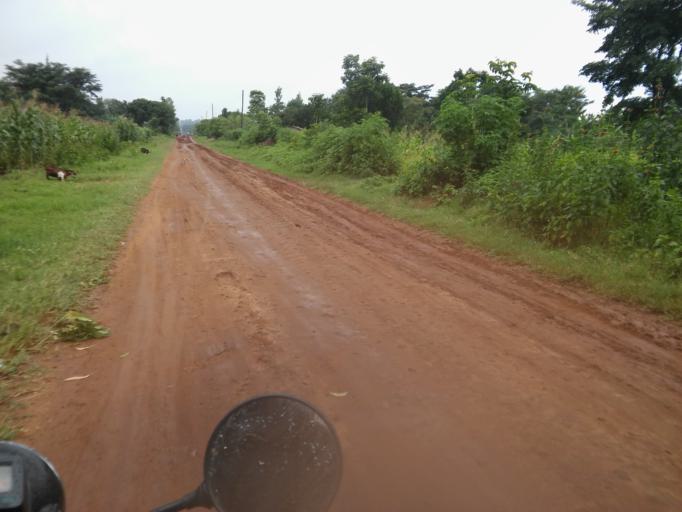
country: UG
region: Eastern Region
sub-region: Mbale District
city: Mbale
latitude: 1.0047
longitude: 34.1910
